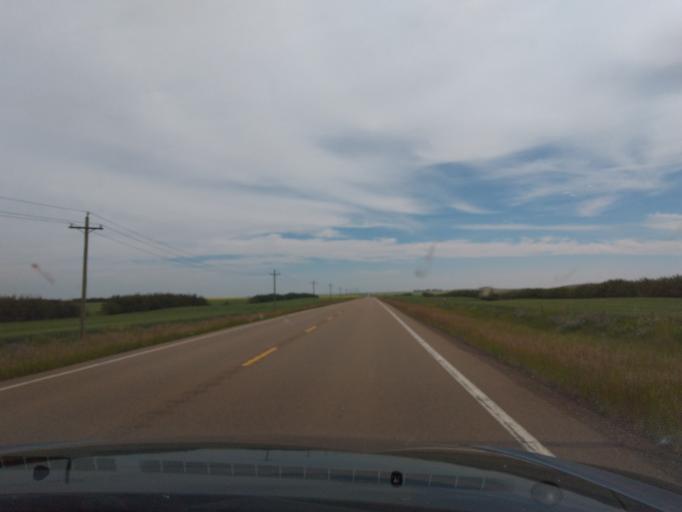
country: CA
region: Alberta
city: Three Hills
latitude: 51.5032
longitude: -112.9680
